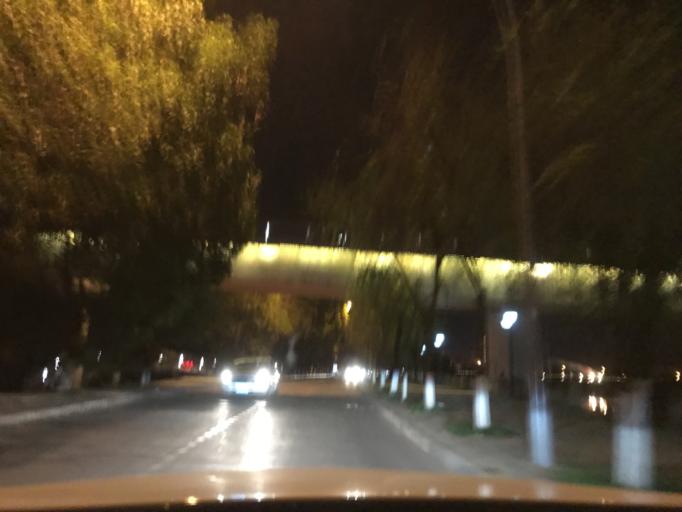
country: CN
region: Sichuan
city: Mianyang
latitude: 31.4592
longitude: 104.7459
